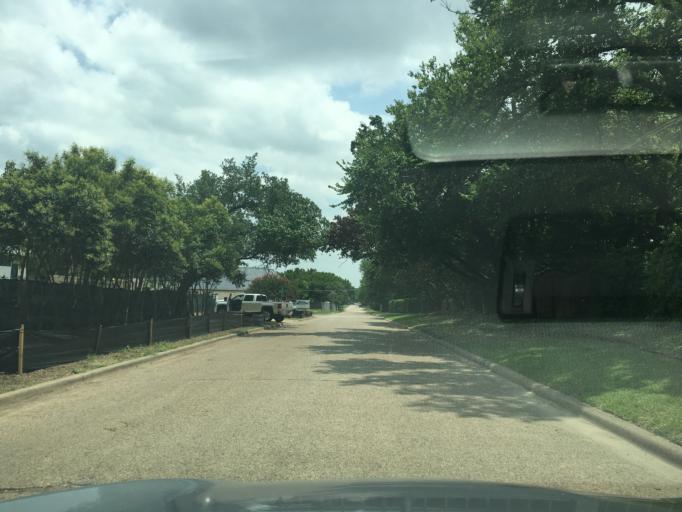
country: US
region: Texas
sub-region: Dallas County
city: University Park
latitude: 32.8940
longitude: -96.8297
